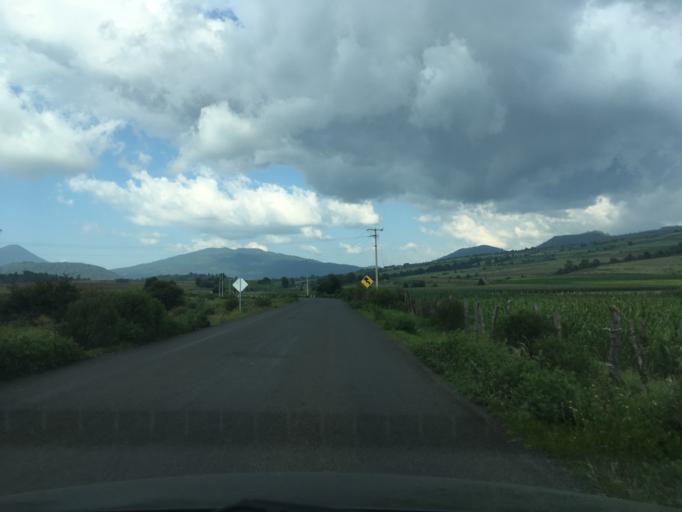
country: MX
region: Michoacan
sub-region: Nahuatzen
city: Sevina
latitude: 19.6041
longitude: -101.9482
